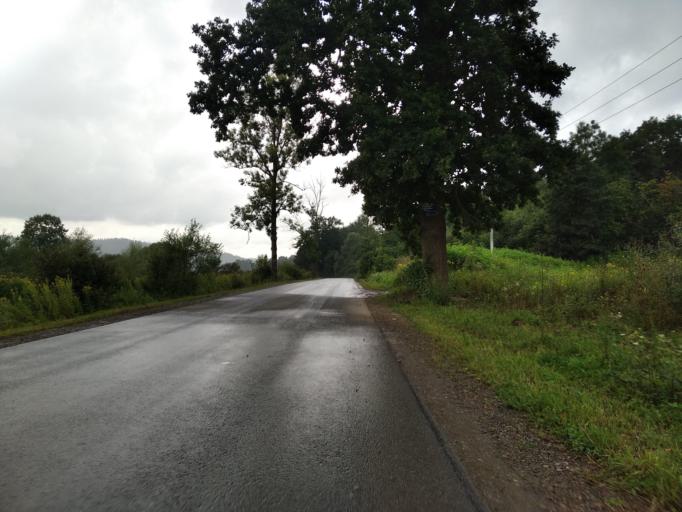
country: PL
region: Subcarpathian Voivodeship
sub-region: Powiat brzozowski
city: Dydnia
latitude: 49.6795
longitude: 22.2672
